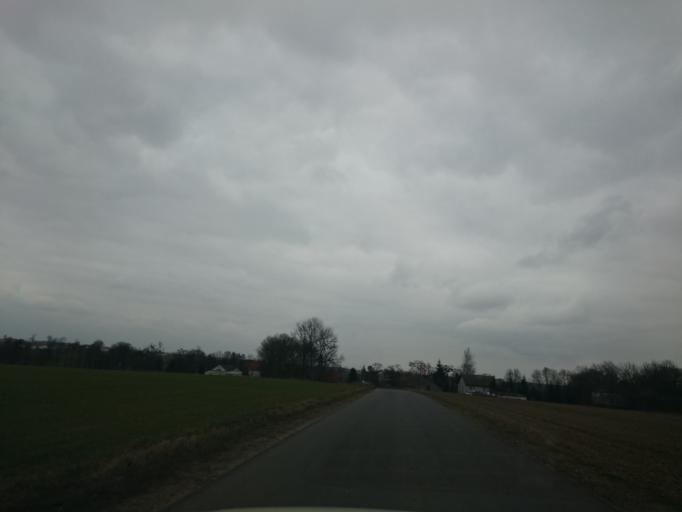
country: PL
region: Kujawsko-Pomorskie
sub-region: Powiat golubsko-dobrzynski
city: Ciechocin
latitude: 53.0471
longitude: 18.8987
